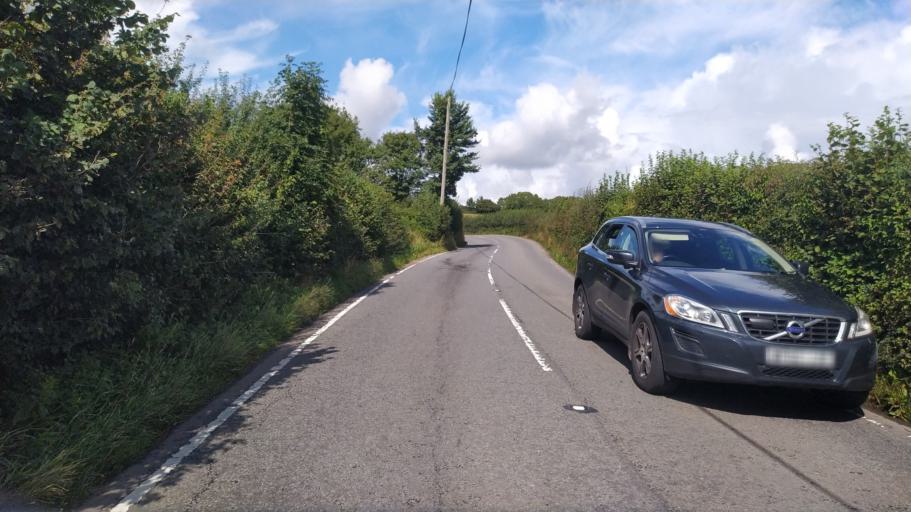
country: GB
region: England
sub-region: Dorset
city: Stalbridge
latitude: 50.9135
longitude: -2.4226
